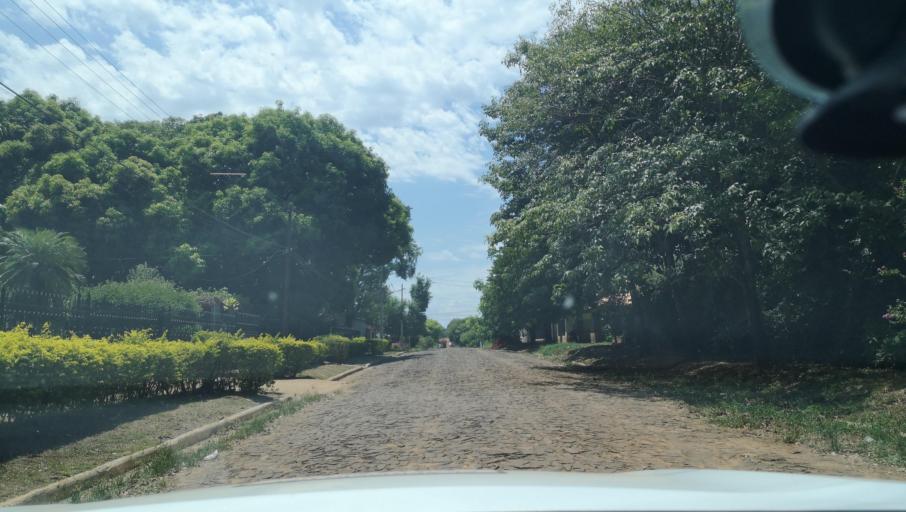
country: PY
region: Itapua
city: Carmen del Parana
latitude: -27.1650
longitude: -56.2456
